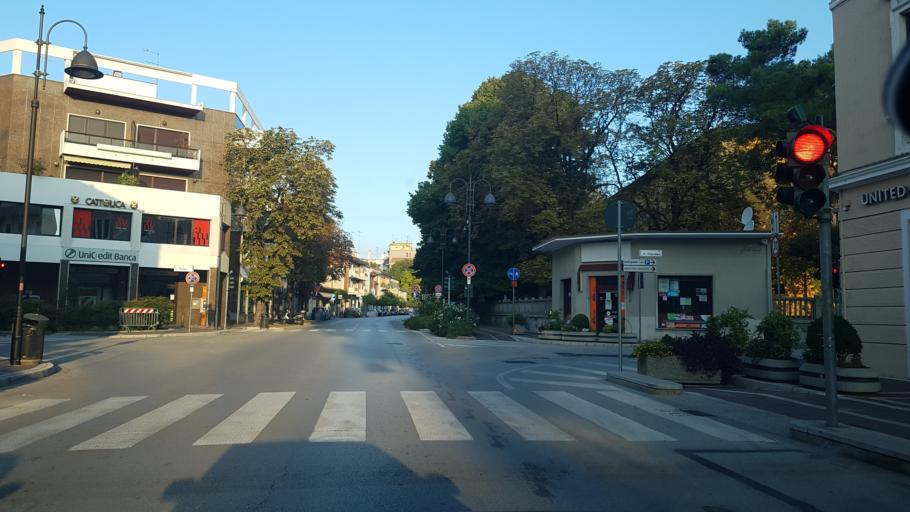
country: IT
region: Friuli Venezia Giulia
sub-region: Provincia di Gorizia
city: Monfalcone
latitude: 45.8094
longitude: 13.5305
